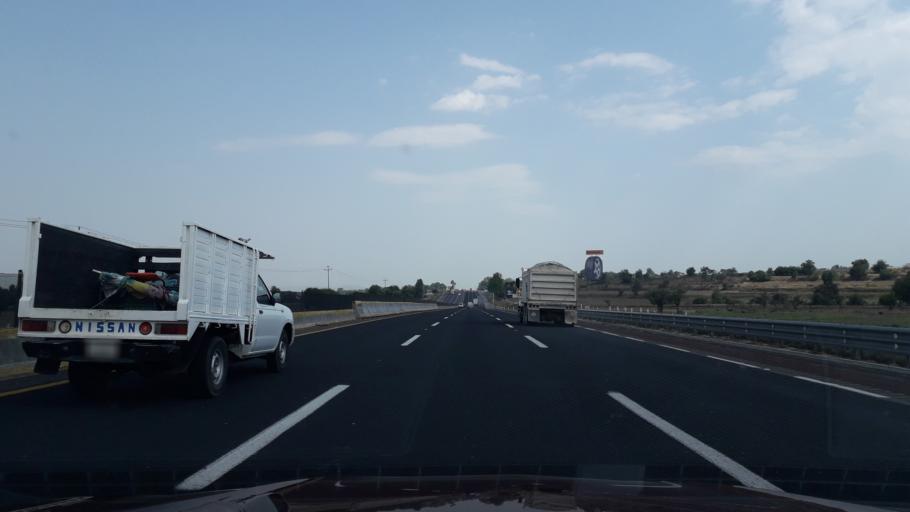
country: MX
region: Puebla
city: San Matias Tlalancaleca
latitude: 19.3123
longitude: -98.5009
